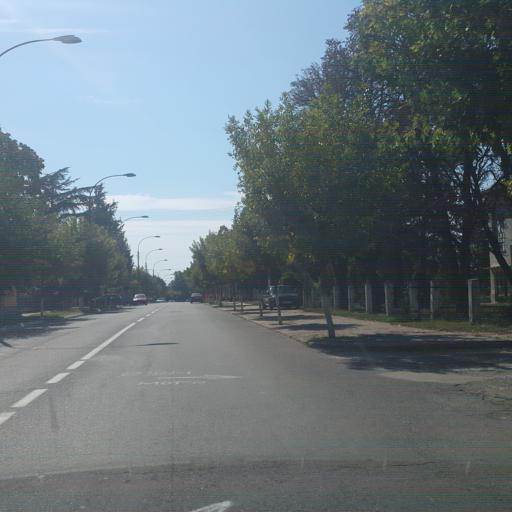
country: RS
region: Central Serbia
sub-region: Zajecarski Okrug
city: Knjazevac
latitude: 43.6851
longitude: 22.2929
